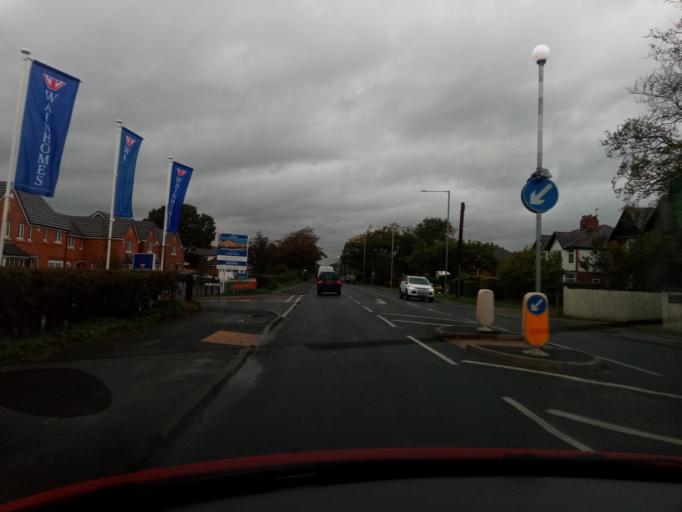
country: GB
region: England
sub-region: Lancashire
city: Preston
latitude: 53.8226
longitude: -2.7350
